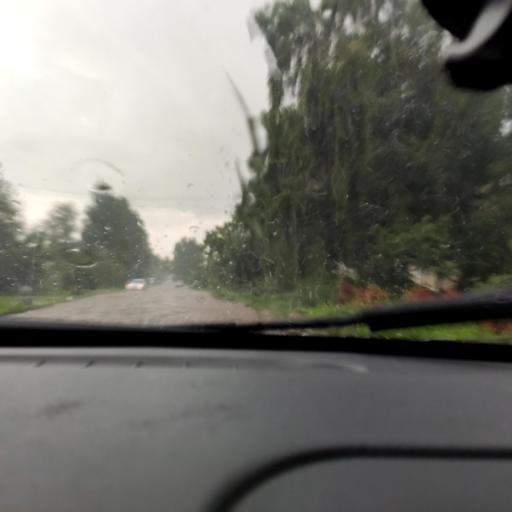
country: RU
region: Voronezj
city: Somovo
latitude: 51.7415
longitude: 39.2714
